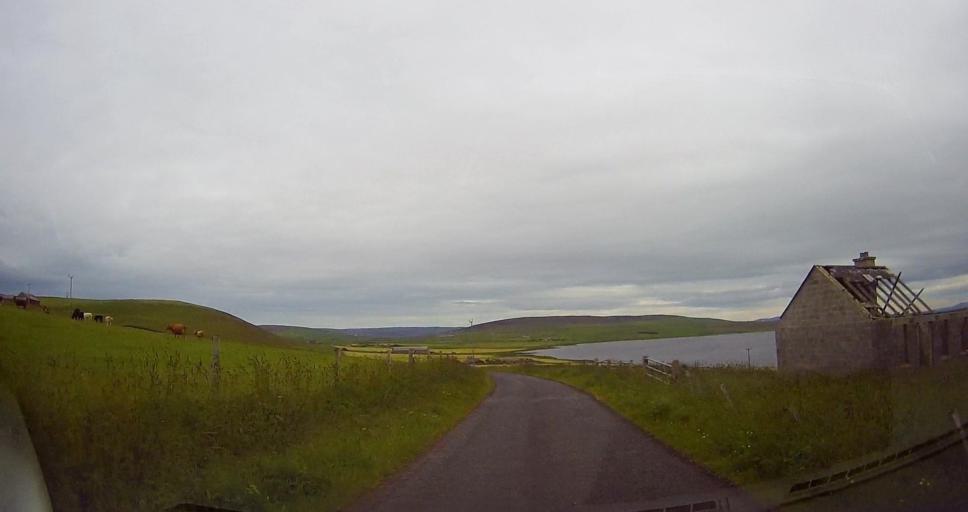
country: GB
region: Scotland
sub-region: Orkney Islands
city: Stromness
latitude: 59.1210
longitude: -3.2749
